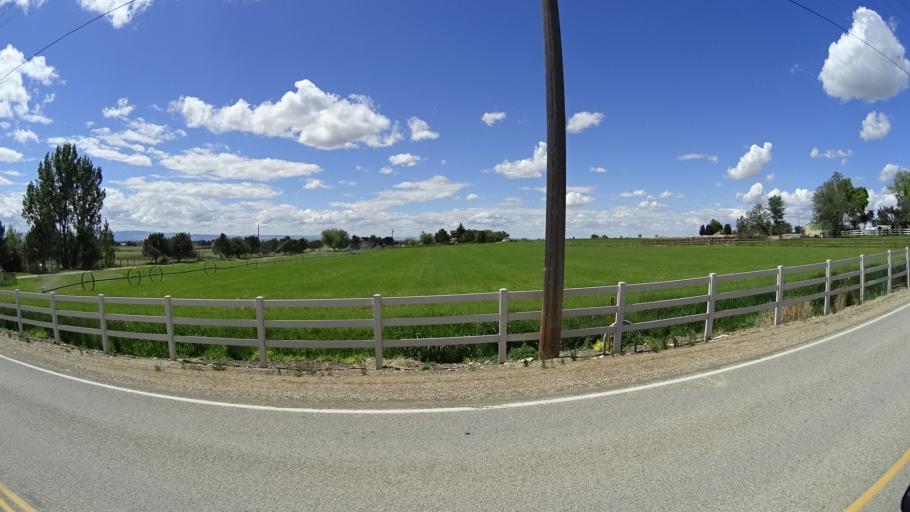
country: US
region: Idaho
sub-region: Ada County
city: Kuna
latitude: 43.5560
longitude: -116.4337
